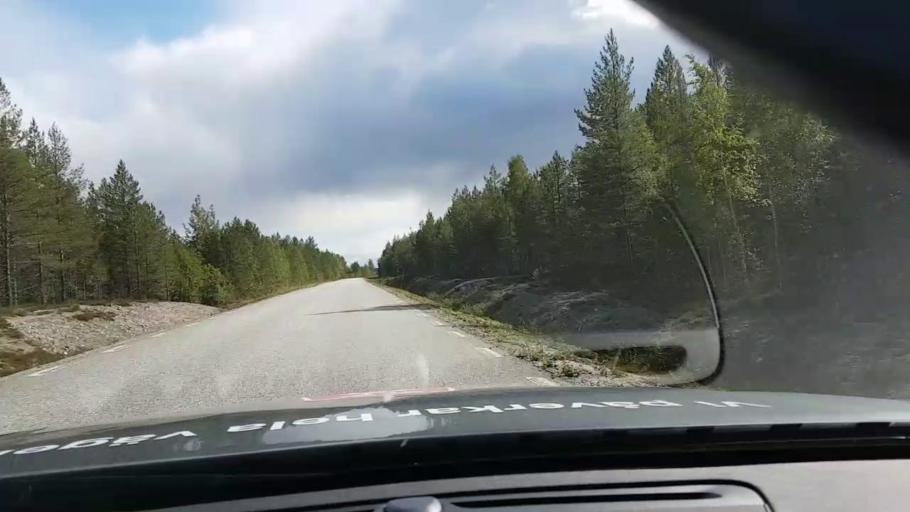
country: SE
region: Vaesterbotten
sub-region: Asele Kommun
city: Asele
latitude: 63.9103
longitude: 17.3381
